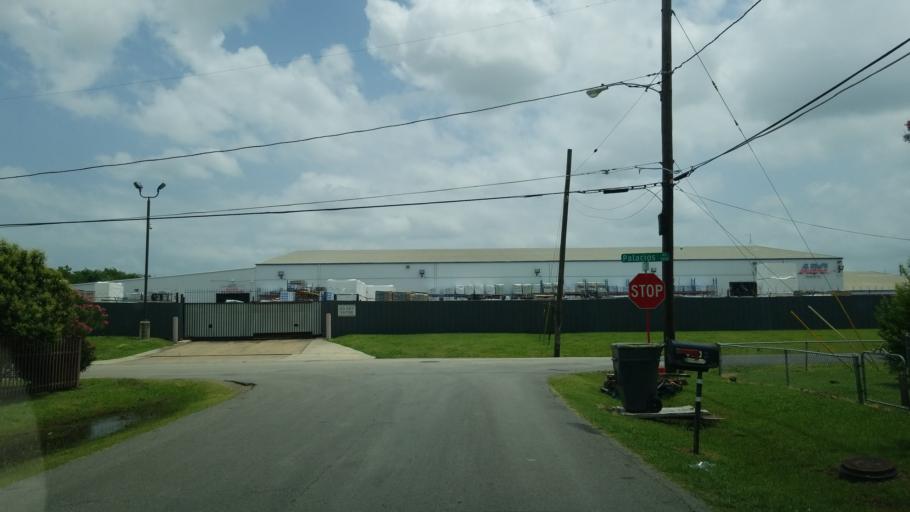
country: US
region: Texas
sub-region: Dallas County
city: Cockrell Hill
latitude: 32.7796
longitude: -96.9014
